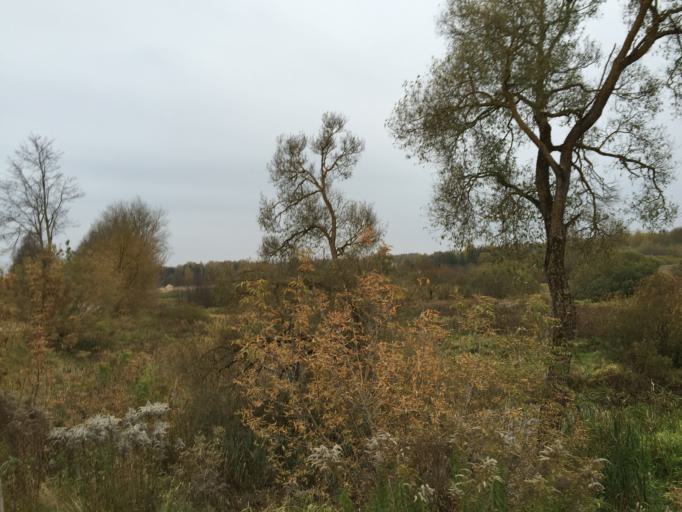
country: LV
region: Jelgava
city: Jelgava
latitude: 56.6378
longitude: 23.7395
